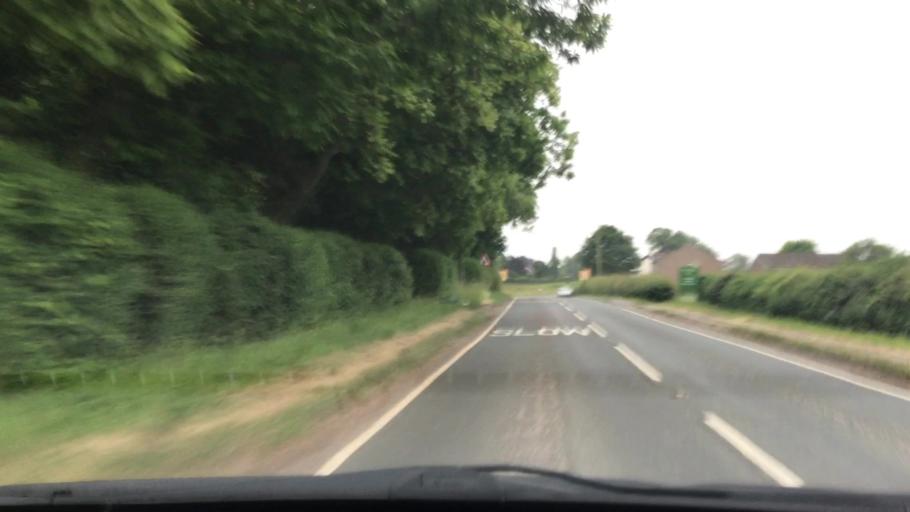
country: GB
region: England
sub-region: City and Borough of Leeds
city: Wetherby
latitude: 53.9532
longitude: -1.3987
